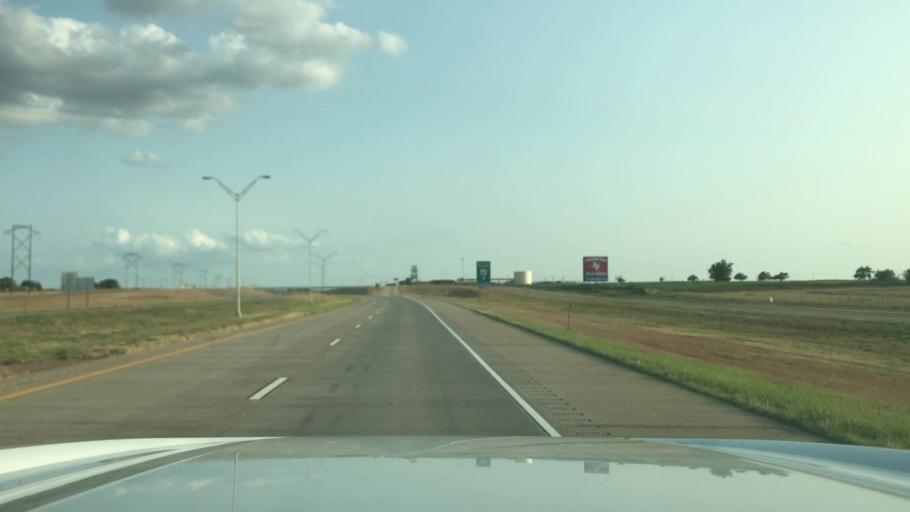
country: US
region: Texas
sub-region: Swisher County
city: Tulia
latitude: 34.5369
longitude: -101.7953
